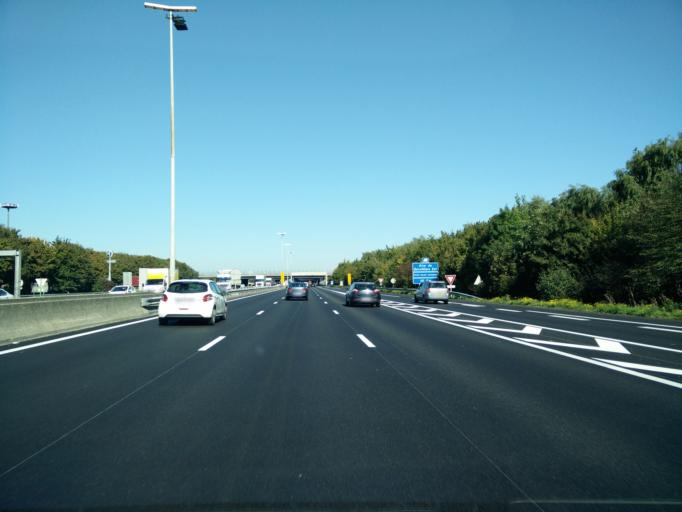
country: FR
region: Ile-de-France
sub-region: Departement du Val-d'Oise
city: Roissy-en-France
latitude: 49.0132
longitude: 2.5303
